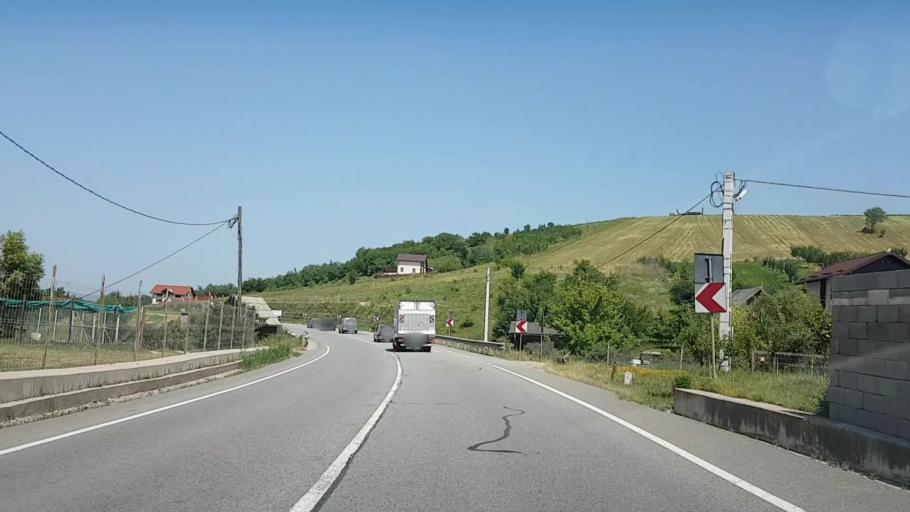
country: RO
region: Cluj
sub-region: Comuna Apahida
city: Dezmir
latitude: 46.7713
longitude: 23.6995
